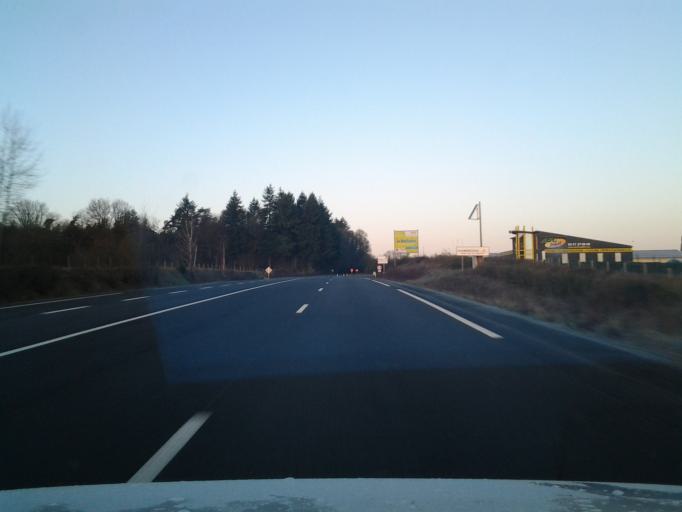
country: FR
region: Pays de la Loire
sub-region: Departement de la Vendee
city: Chambretaud
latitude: 46.9168
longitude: -0.9537
